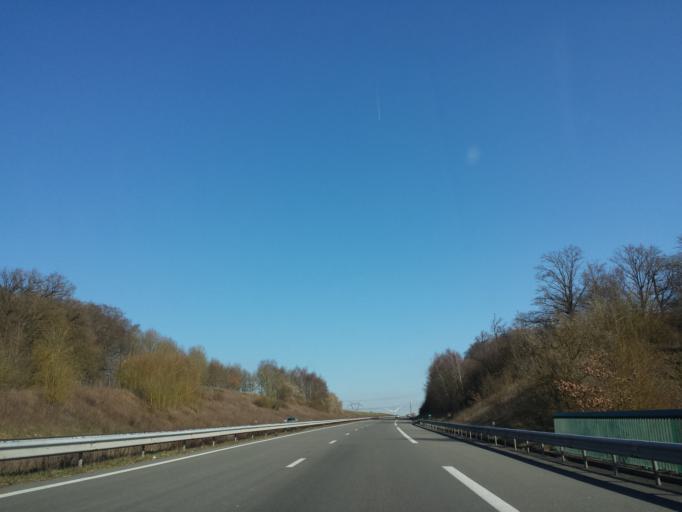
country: FR
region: Picardie
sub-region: Departement de la Somme
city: Conty
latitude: 49.6794
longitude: 2.2146
